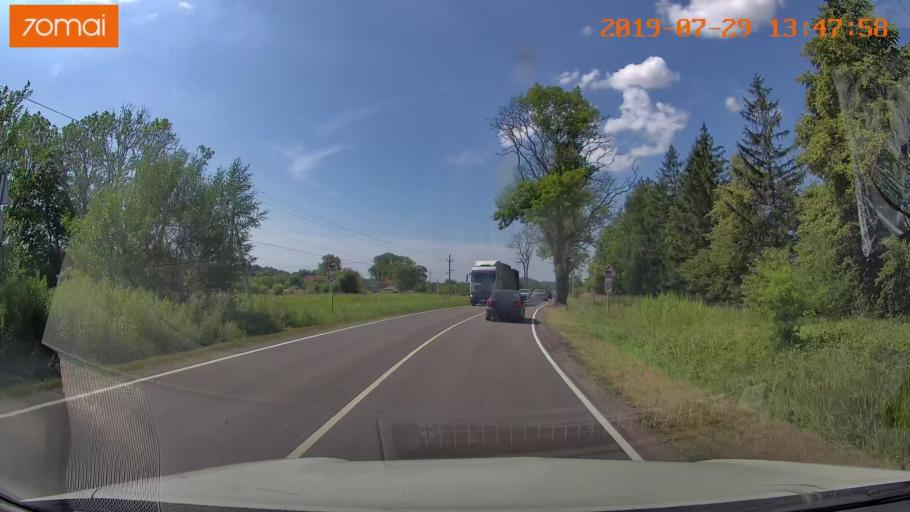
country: RU
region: Kaliningrad
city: Primorsk
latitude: 54.7385
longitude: 20.0401
